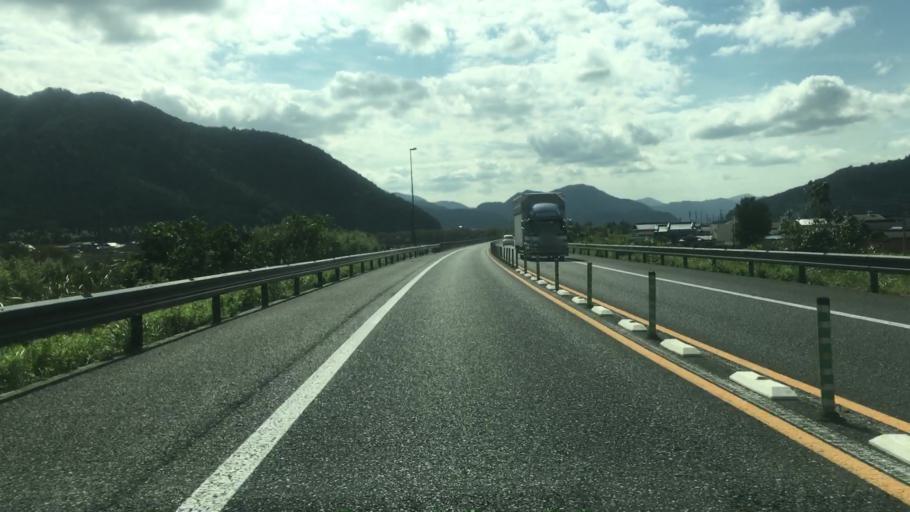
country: JP
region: Kyoto
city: Fukuchiyama
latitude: 35.2236
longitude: 135.0330
